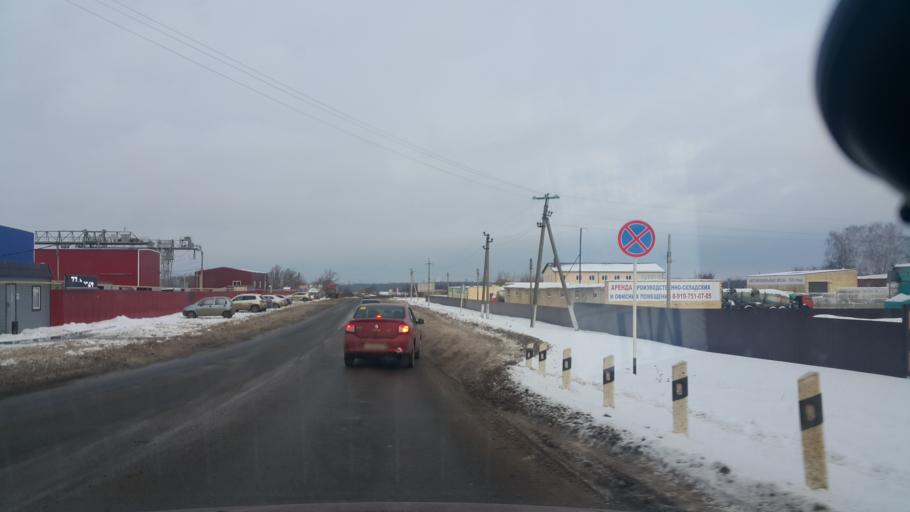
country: RU
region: Tambov
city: Pokrovo-Prigorodnoye
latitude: 52.6590
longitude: 41.4313
